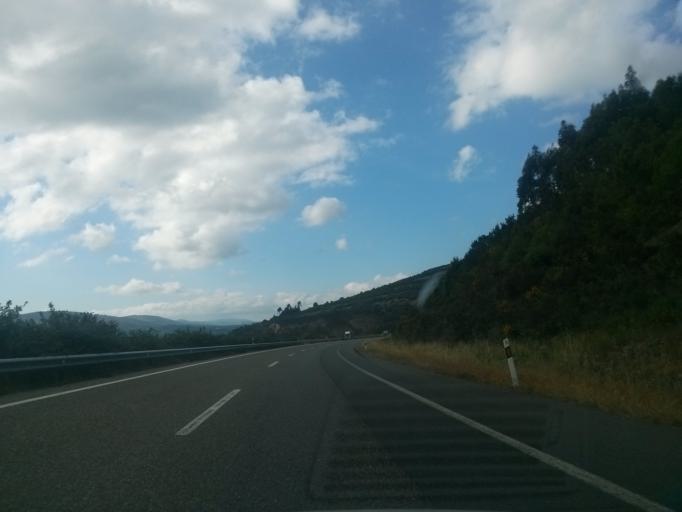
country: ES
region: Galicia
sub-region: Provincia de Lugo
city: Becerrea
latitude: 42.9034
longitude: -7.1904
